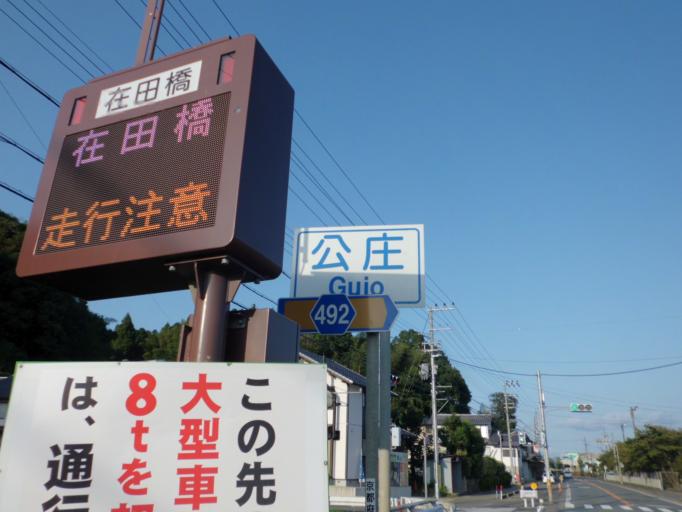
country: JP
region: Kyoto
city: Fukuchiyama
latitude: 35.3715
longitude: 135.1271
